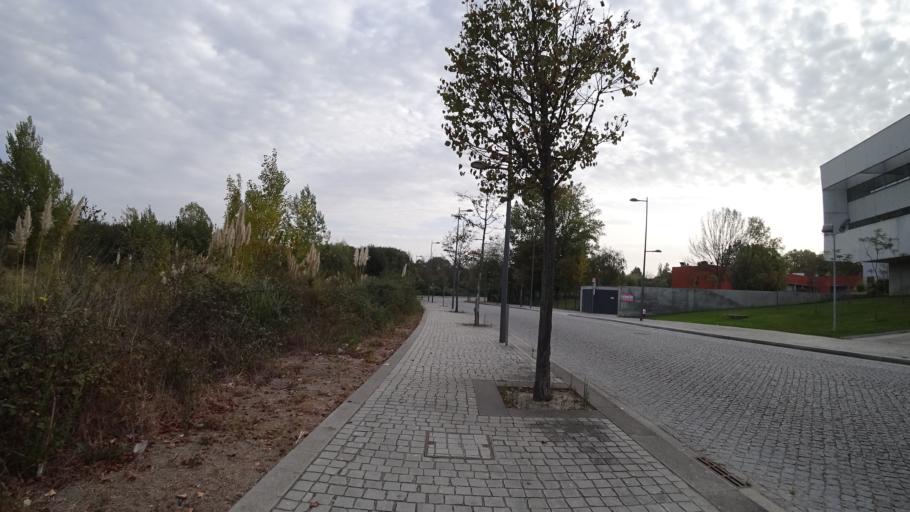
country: PT
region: Porto
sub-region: Matosinhos
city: Sao Mamede de Infesta
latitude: 41.1765
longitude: -8.6035
